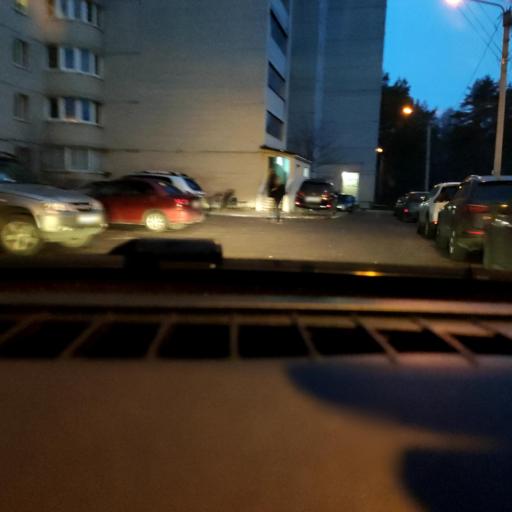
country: RU
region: Voronezj
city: Podgornoye
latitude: 51.7273
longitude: 39.1769
